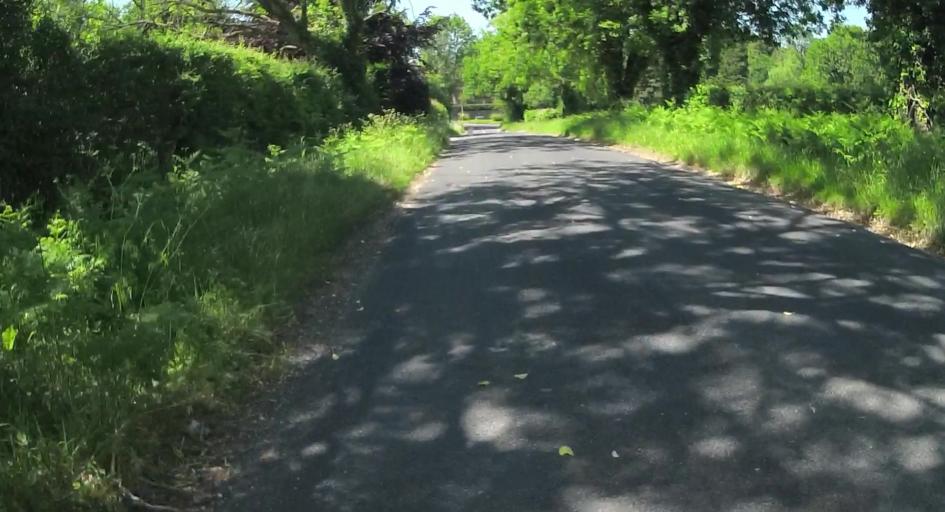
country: GB
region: England
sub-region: Hampshire
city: Kingsclere
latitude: 51.3464
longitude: -1.2055
